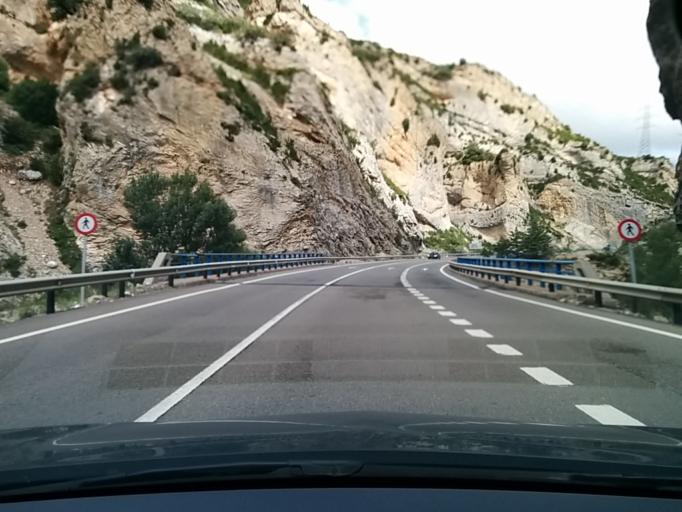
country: ES
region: Aragon
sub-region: Provincia de Huesca
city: Arguis
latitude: 42.3003
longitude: -0.4280
